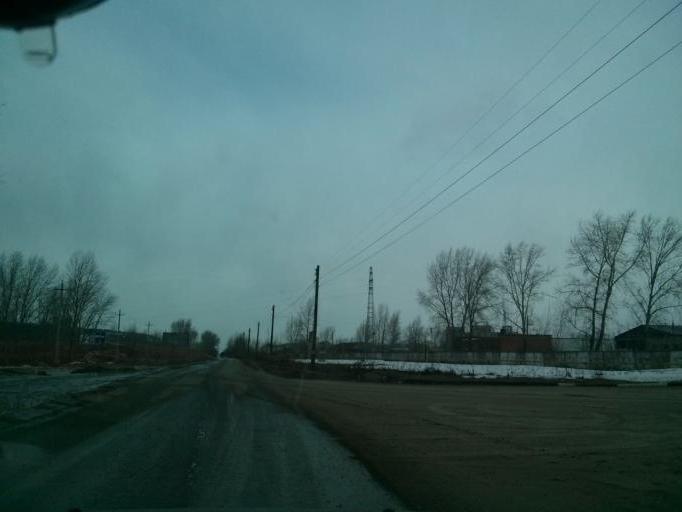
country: RU
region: Nizjnij Novgorod
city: Afonino
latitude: 56.2857
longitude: 44.1193
